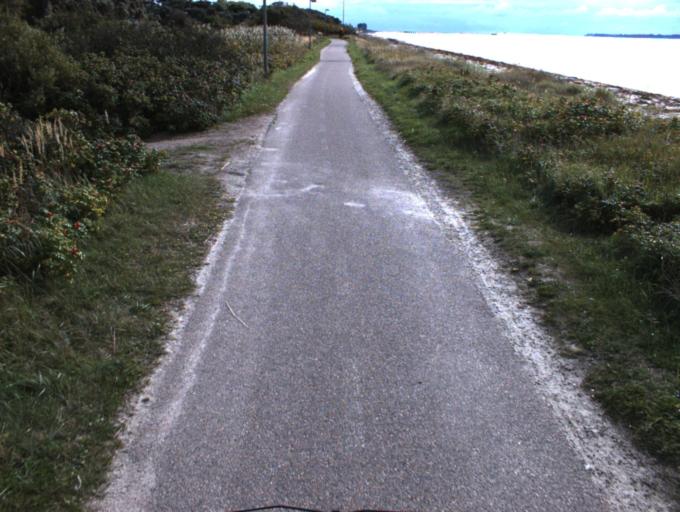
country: SE
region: Skane
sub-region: Helsingborg
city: Rydeback
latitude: 55.9755
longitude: 12.7559
